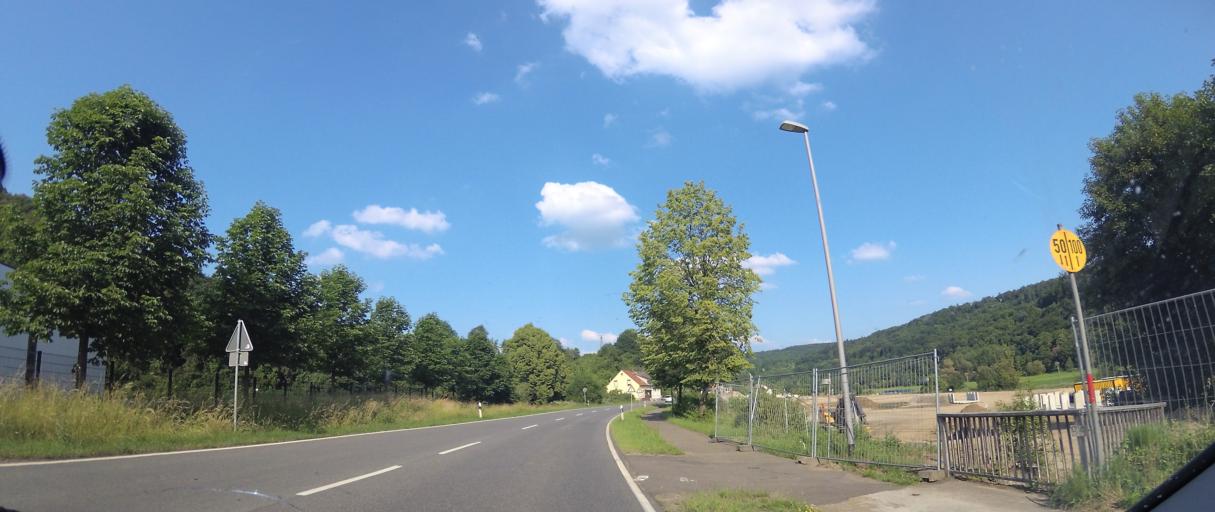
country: DE
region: Rheinland-Pfalz
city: Medard
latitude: 49.6663
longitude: 7.6024
